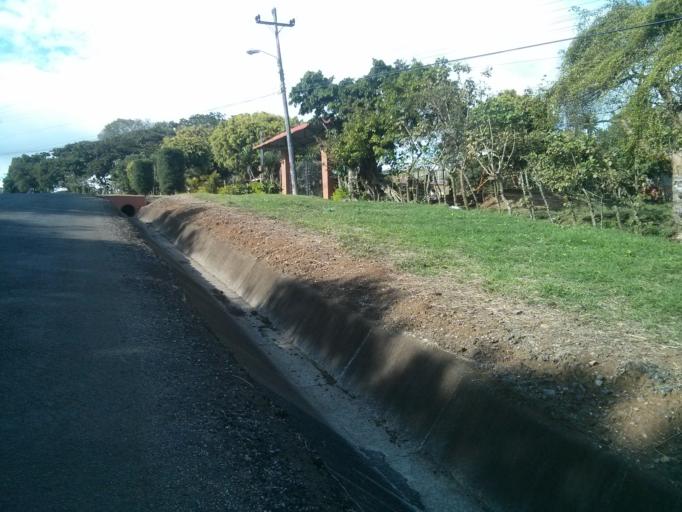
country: CR
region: Cartago
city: Cartago
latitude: 9.9019
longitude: -83.9414
